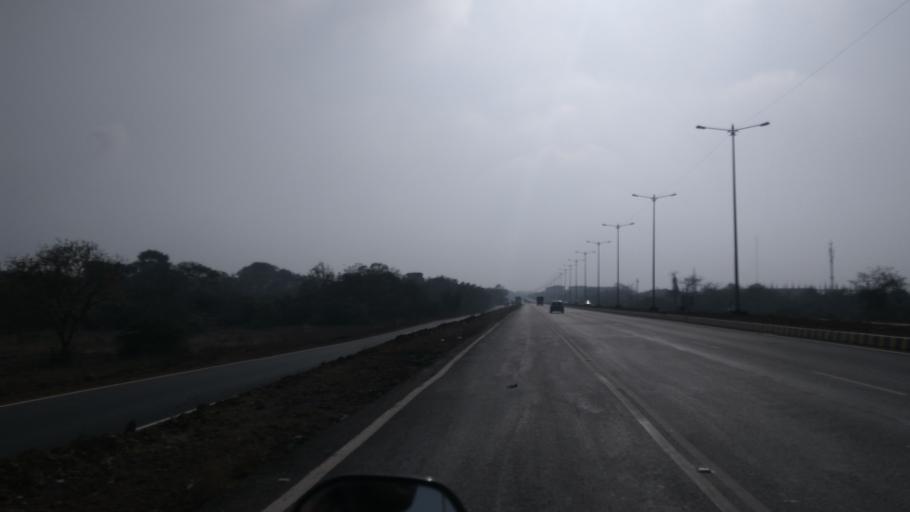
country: IN
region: Goa
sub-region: North Goa
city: Bambolim
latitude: 15.4932
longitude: 73.8844
